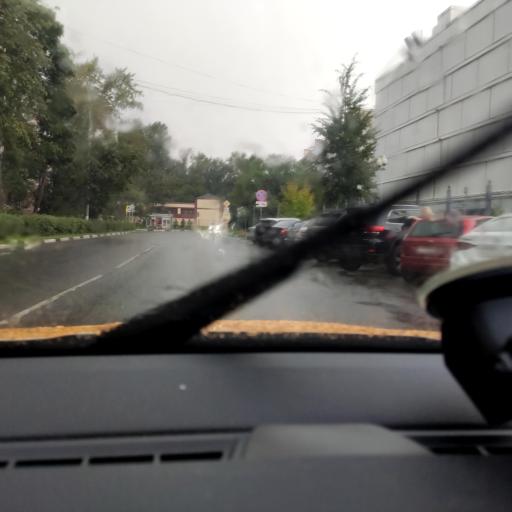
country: RU
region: Moskovskaya
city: Mytishchi
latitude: 55.9098
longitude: 37.7275
